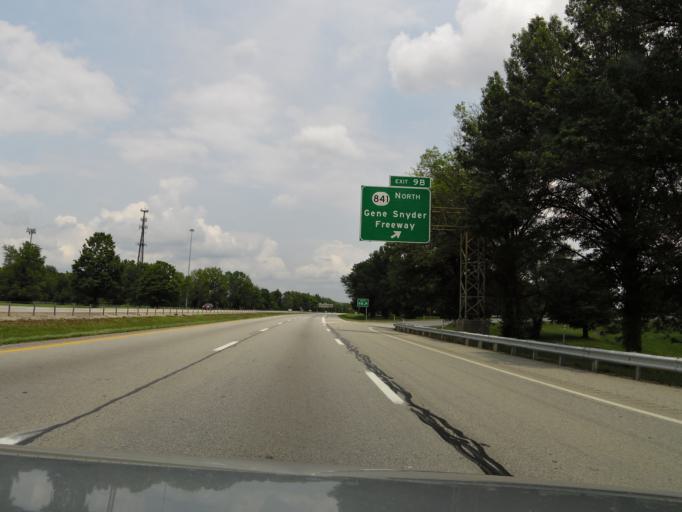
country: US
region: Kentucky
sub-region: Jefferson County
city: Worthington
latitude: 38.3151
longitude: -85.5810
